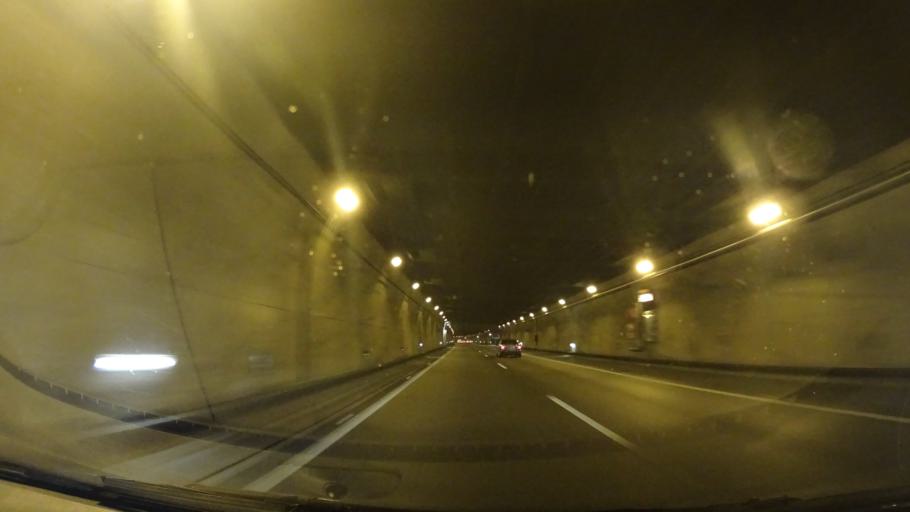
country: ES
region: Madrid
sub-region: Provincia de Madrid
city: Guadarrama
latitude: 40.7164
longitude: -4.1536
